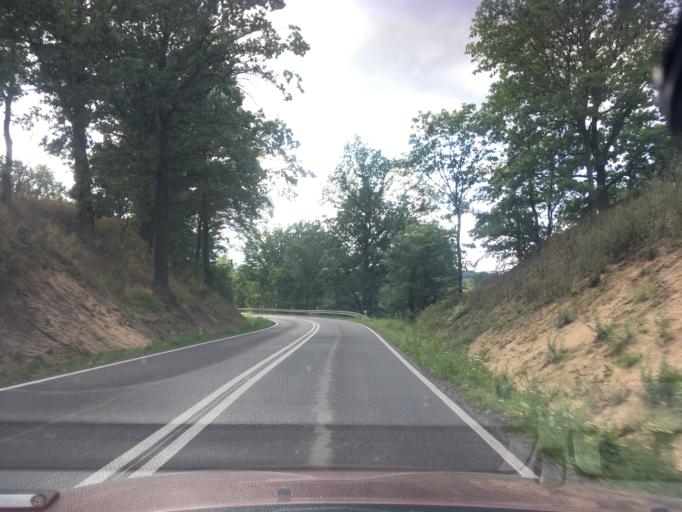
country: PL
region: Lower Silesian Voivodeship
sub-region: Powiat zgorzelecki
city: Piensk
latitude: 51.2125
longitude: 15.0202
